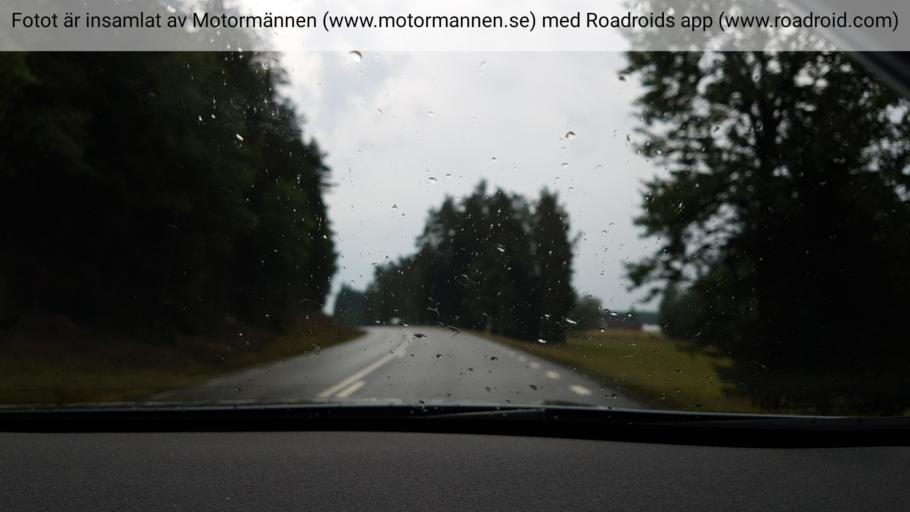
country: SE
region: Joenkoeping
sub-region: Vaggeryds Kommun
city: Vaggeryd
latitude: 57.4616
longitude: 14.3148
